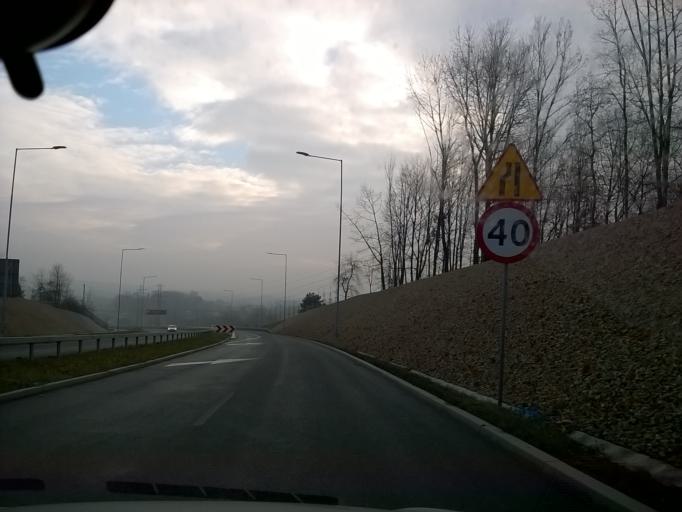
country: PL
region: Silesian Voivodeship
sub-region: Ruda Slaska
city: Ruda Slaska
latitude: 50.2781
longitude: 18.8453
